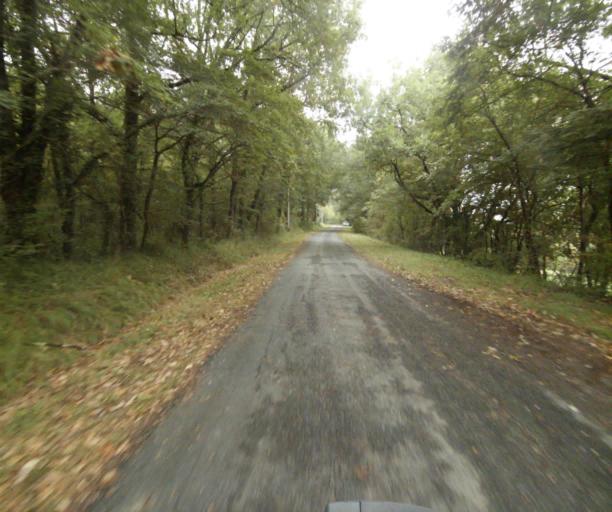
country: FR
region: Midi-Pyrenees
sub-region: Departement de la Haute-Garonne
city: Villemur-sur-Tarn
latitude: 43.8914
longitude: 1.4814
